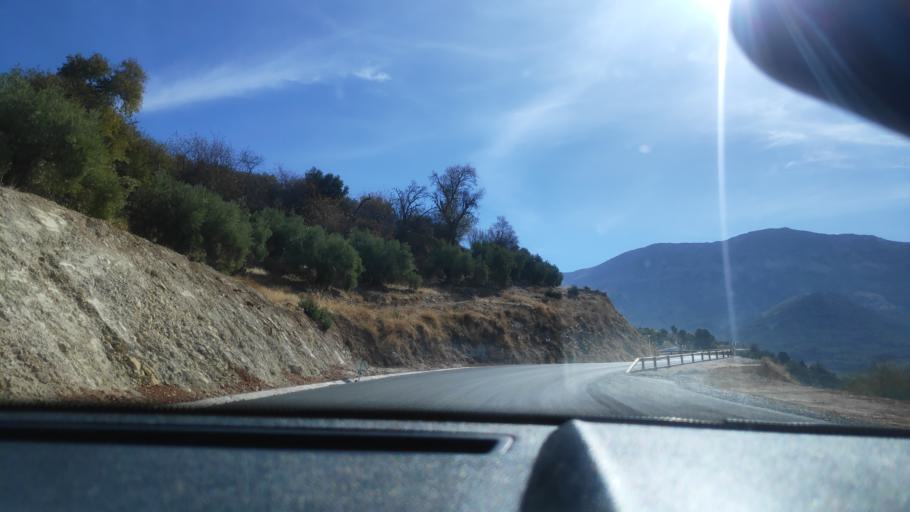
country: ES
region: Andalusia
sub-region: Provincia de Jaen
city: Torres
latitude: 37.7787
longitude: -3.5028
